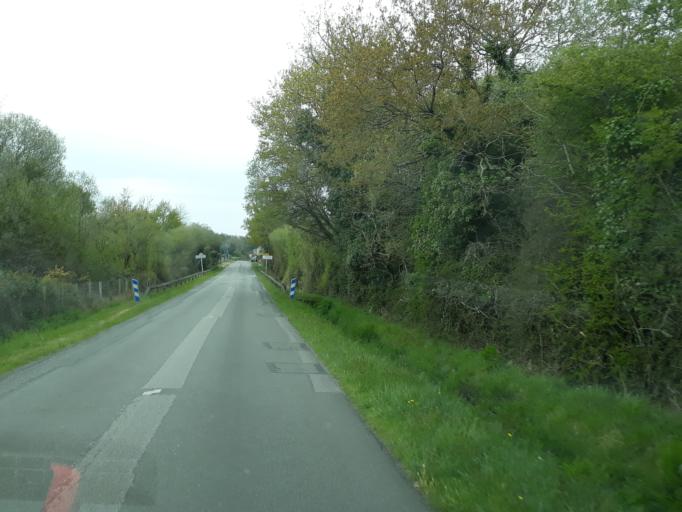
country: FR
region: Brittany
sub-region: Departement du Morbihan
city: Theix
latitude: 47.6191
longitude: -2.6812
